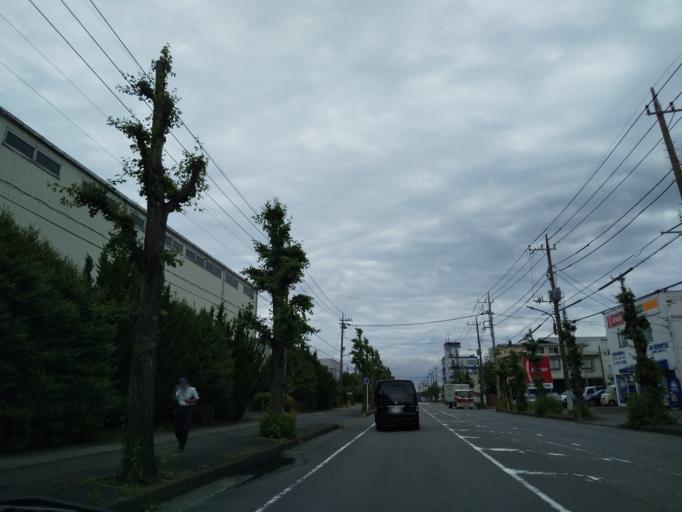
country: JP
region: Kanagawa
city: Zama
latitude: 35.5095
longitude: 139.3531
